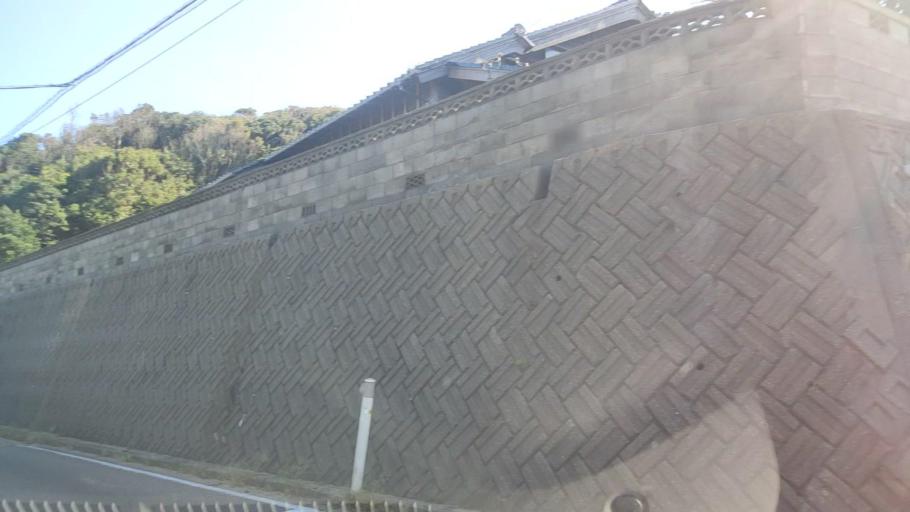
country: JP
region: Ishikawa
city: Hakui
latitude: 36.9479
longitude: 136.7644
